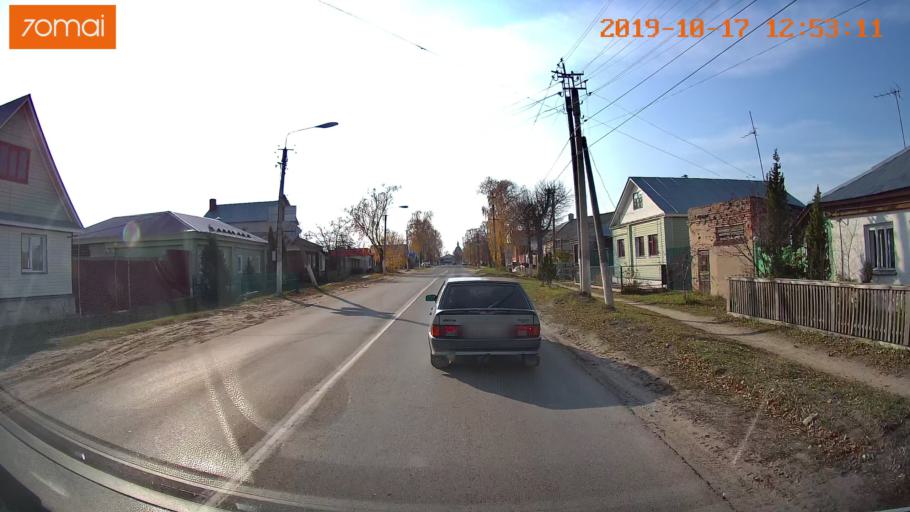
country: RU
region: Rjazan
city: Kasimov
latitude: 54.9439
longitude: 41.3856
